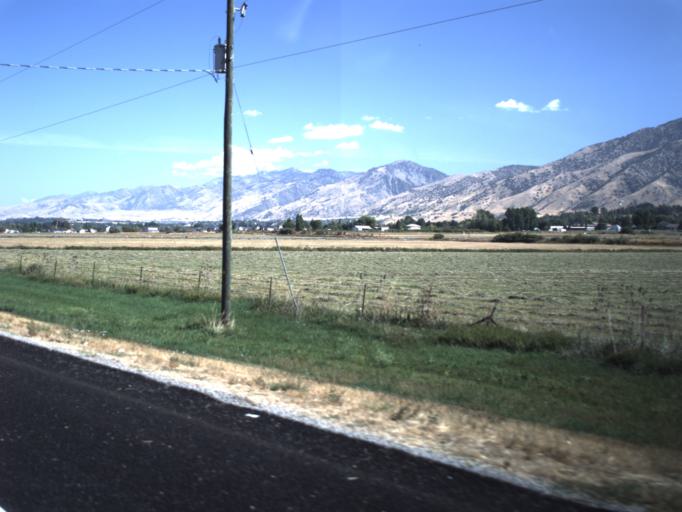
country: US
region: Utah
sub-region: Cache County
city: Millville
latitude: 41.6881
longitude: -111.8339
